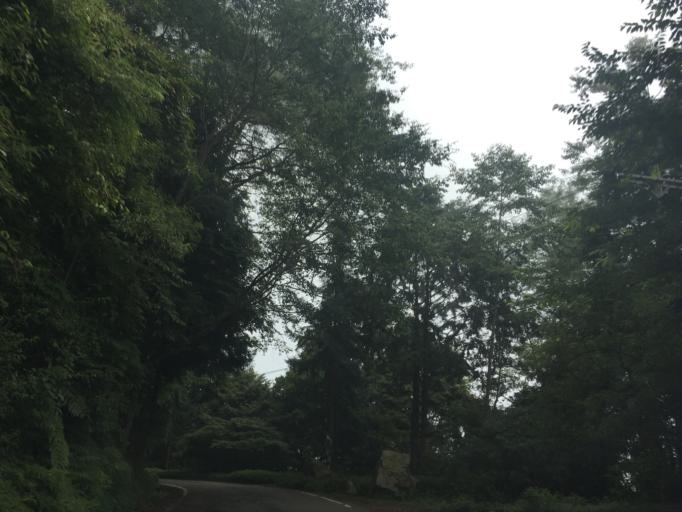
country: TW
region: Taiwan
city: Fengyuan
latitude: 24.2309
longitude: 120.9649
